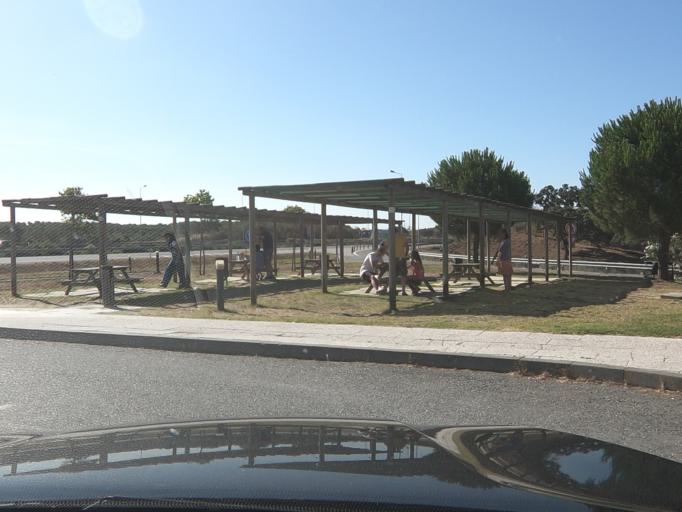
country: PT
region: Beja
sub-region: Ourique
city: Ourique
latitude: 37.5352
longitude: -8.1843
